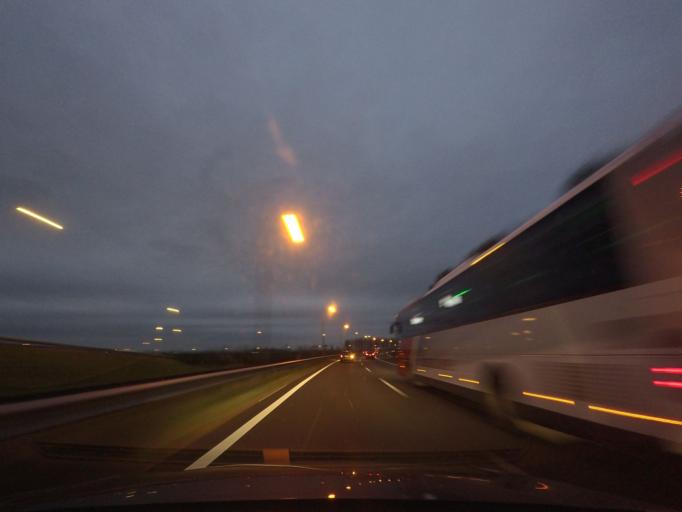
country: NL
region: Utrecht
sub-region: Gemeente Vianen
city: Vianen
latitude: 51.9768
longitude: 5.0993
